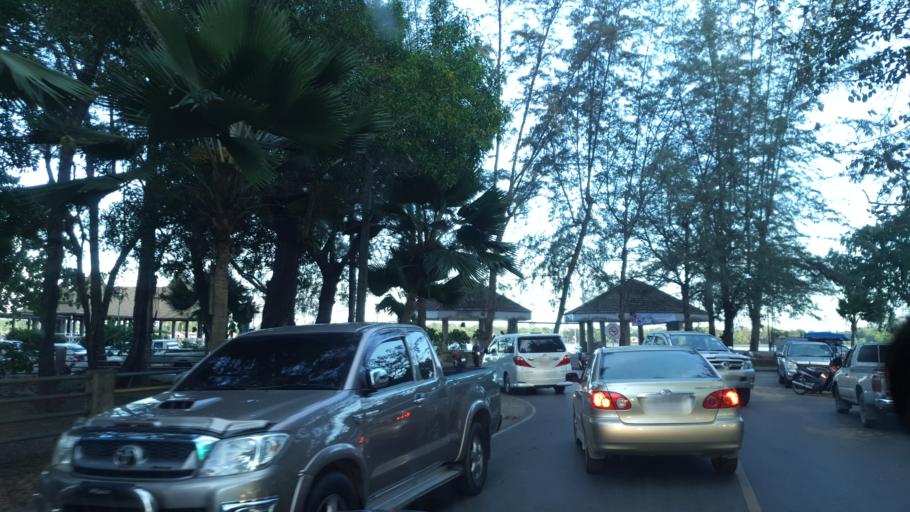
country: TH
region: Krabi
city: Krabi
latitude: 8.0529
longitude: 98.9193
